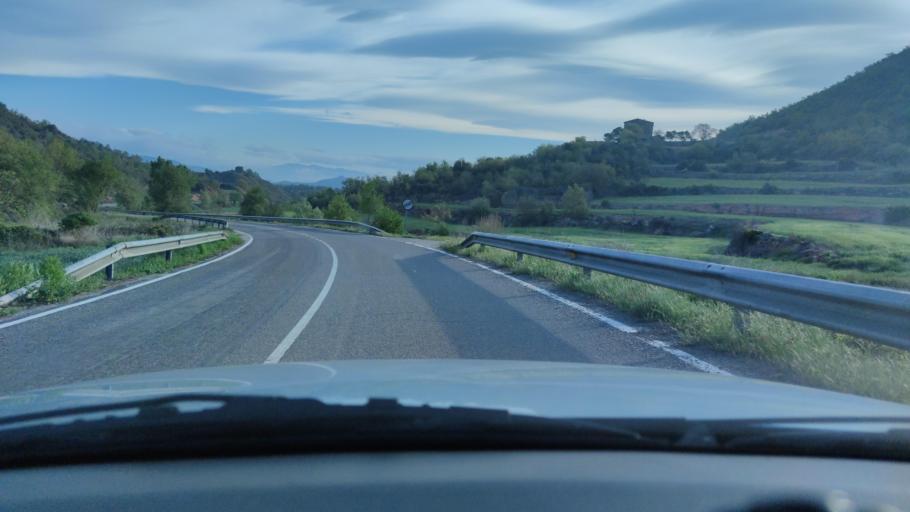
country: ES
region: Catalonia
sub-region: Provincia de Lleida
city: Ponts
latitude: 41.8803
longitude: 1.1811
